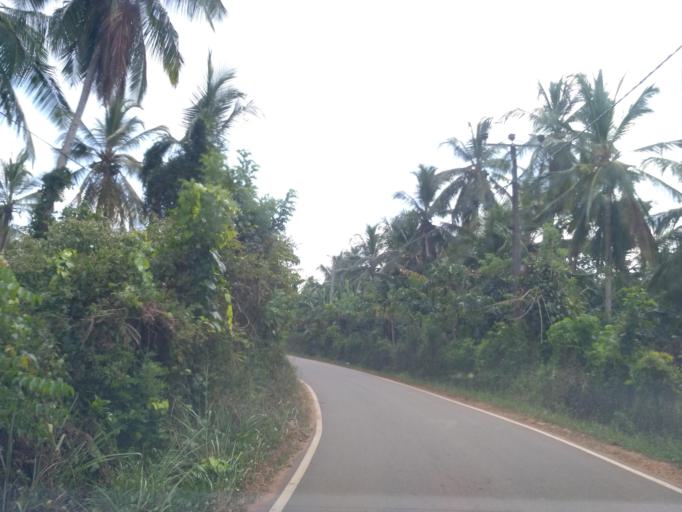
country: LK
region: North Western
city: Kuliyapitiya
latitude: 7.3347
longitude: 80.0619
